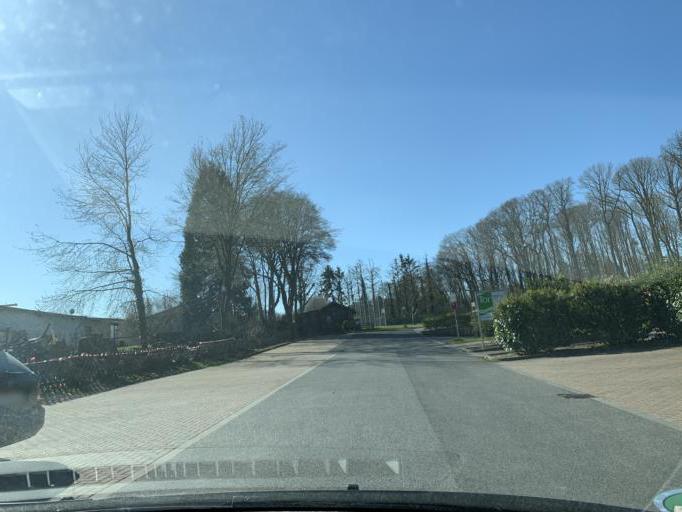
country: DE
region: North Rhine-Westphalia
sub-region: Regierungsbezirk Koln
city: Nideggen
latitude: 50.6859
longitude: 6.4831
